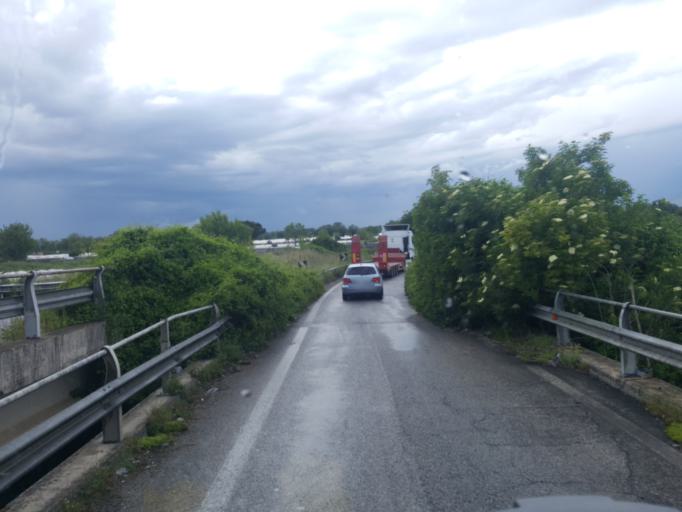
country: IT
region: Campania
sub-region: Provincia di Napoli
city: Pascarola
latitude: 40.9719
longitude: 14.2916
